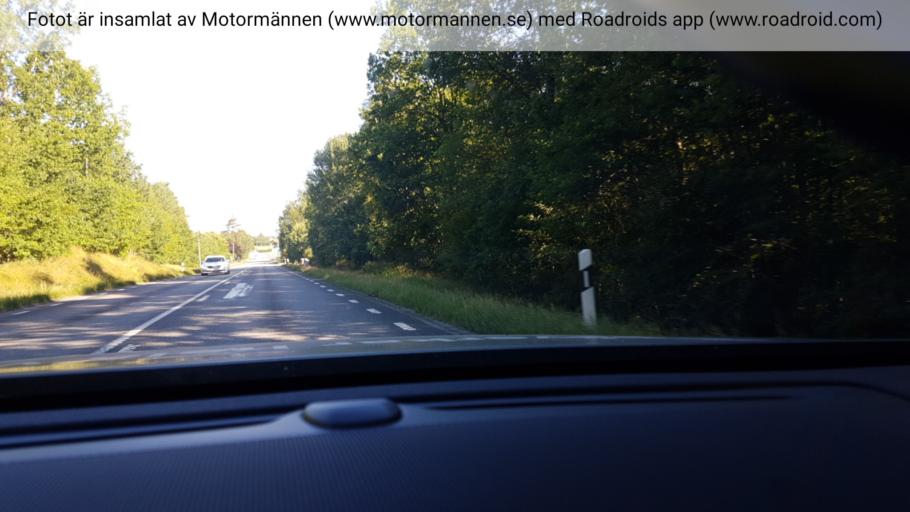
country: SE
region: Kronoberg
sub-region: Markaryds Kommun
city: Markaryd
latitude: 56.4407
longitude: 13.6081
